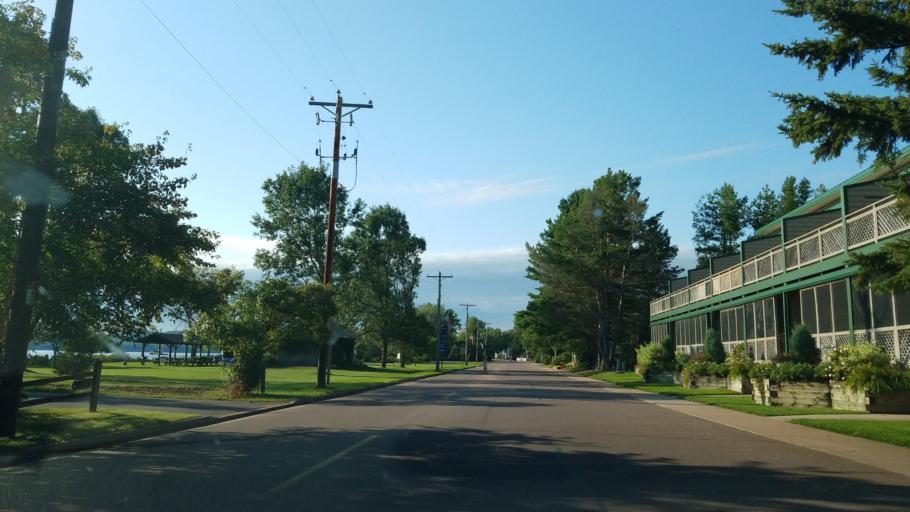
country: US
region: Wisconsin
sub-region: Bayfield County
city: Washburn
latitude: 46.7745
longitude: -90.7828
